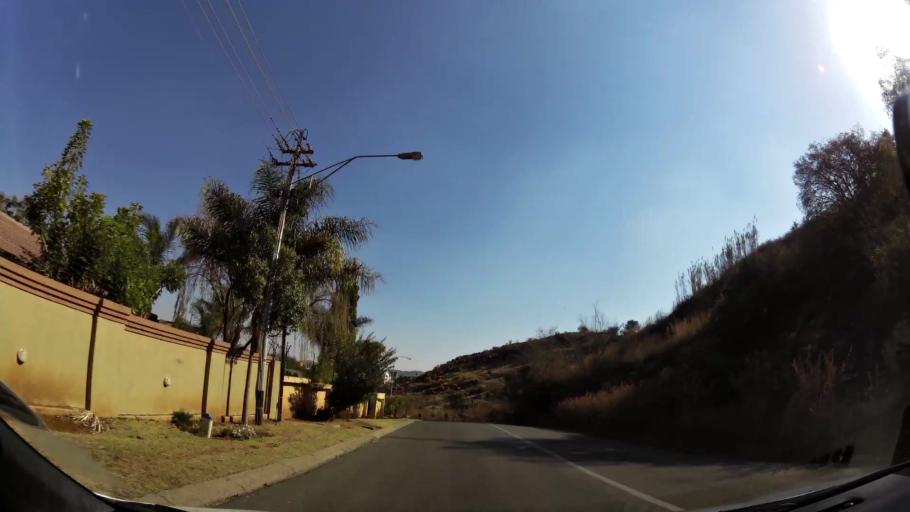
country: ZA
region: Gauteng
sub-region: City of Johannesburg Metropolitan Municipality
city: Johannesburg
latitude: -26.2642
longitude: 28.0412
